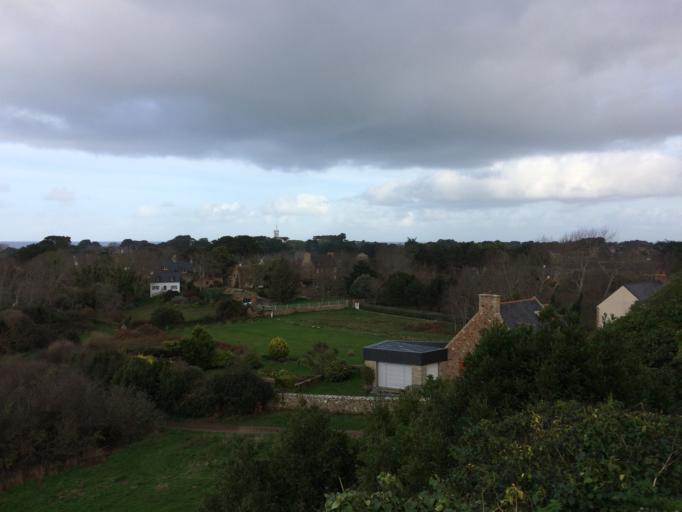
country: FR
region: Brittany
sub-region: Departement des Cotes-d'Armor
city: Ploubazlanec
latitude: 48.8485
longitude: -3.0069
